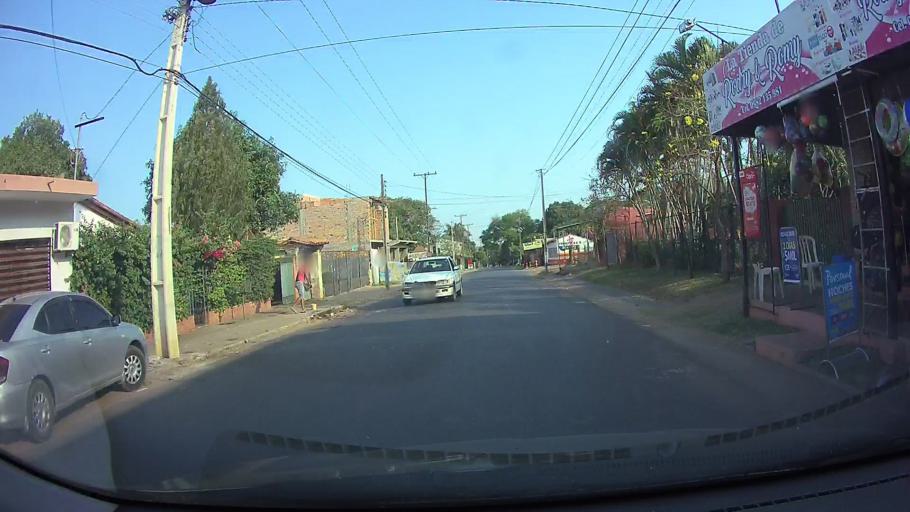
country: PY
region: Central
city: Limpio
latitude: -25.1991
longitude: -57.5070
